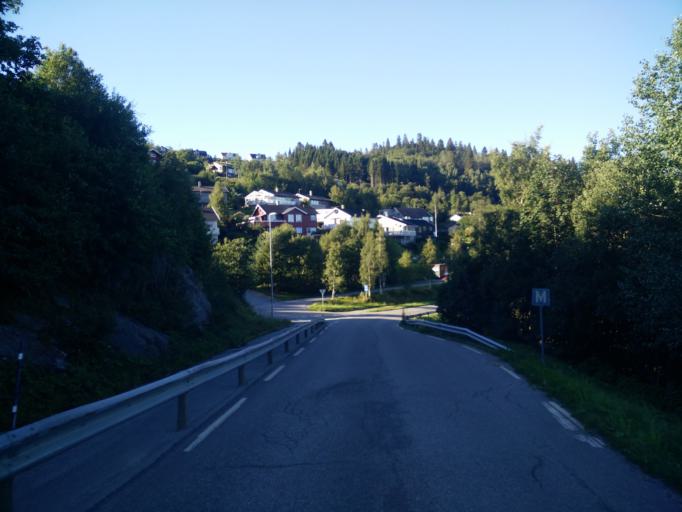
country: NO
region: Sor-Trondelag
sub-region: Skaun
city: Borsa
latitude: 63.3241
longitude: 10.0478
